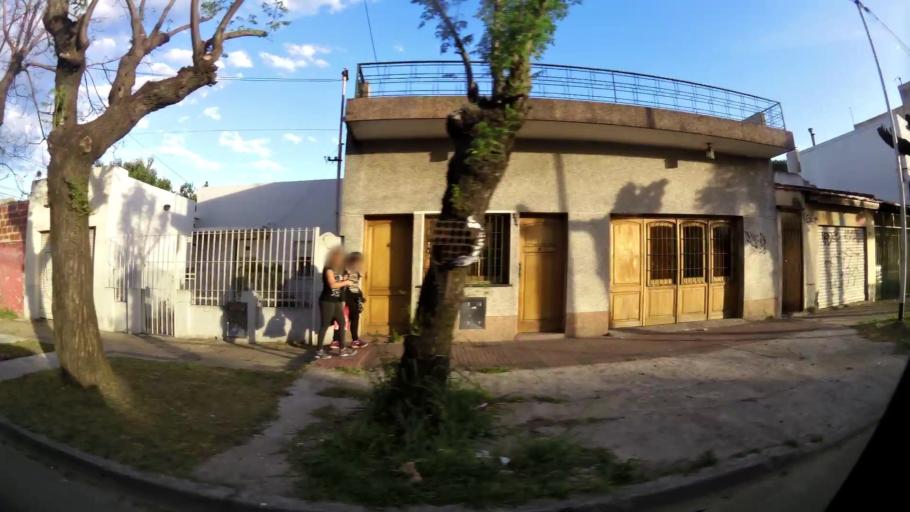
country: AR
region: Buenos Aires
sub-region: Partido de Avellaneda
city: Avellaneda
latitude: -34.6999
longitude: -58.3369
